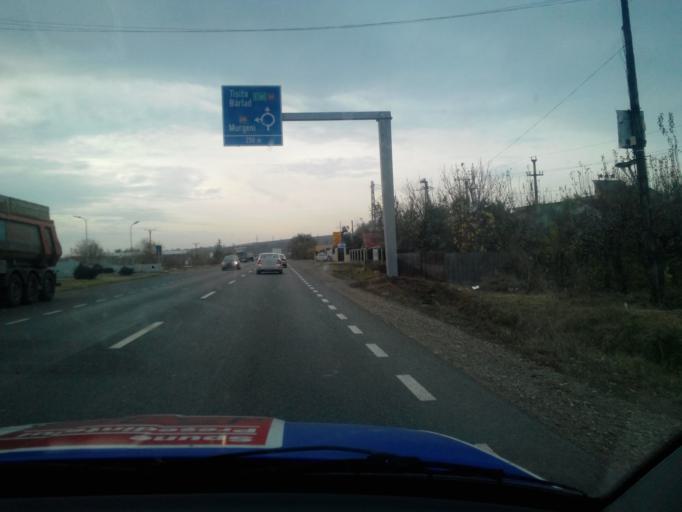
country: RO
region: Vaslui
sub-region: Comuna Zorleni
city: Zorleni
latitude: 46.2669
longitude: 27.6912
